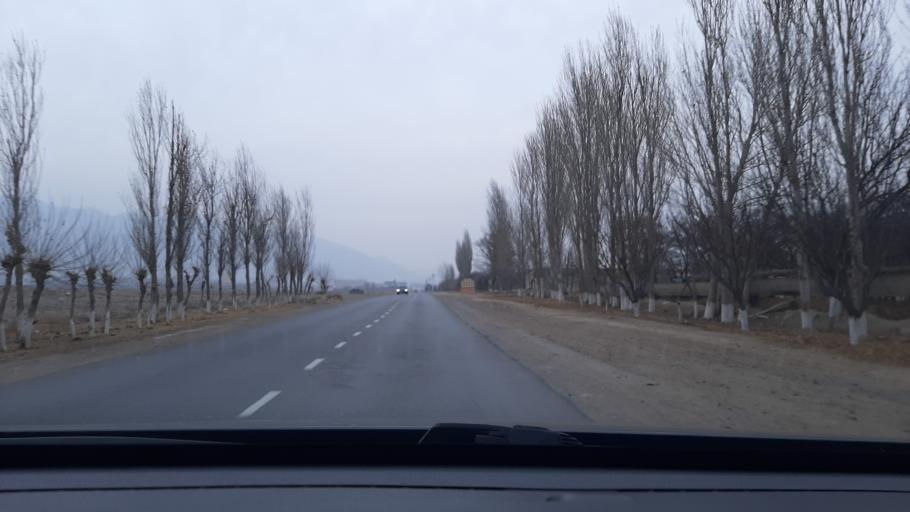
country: TJ
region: Viloyati Sughd
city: Khujand
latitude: 40.2715
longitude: 69.5751
